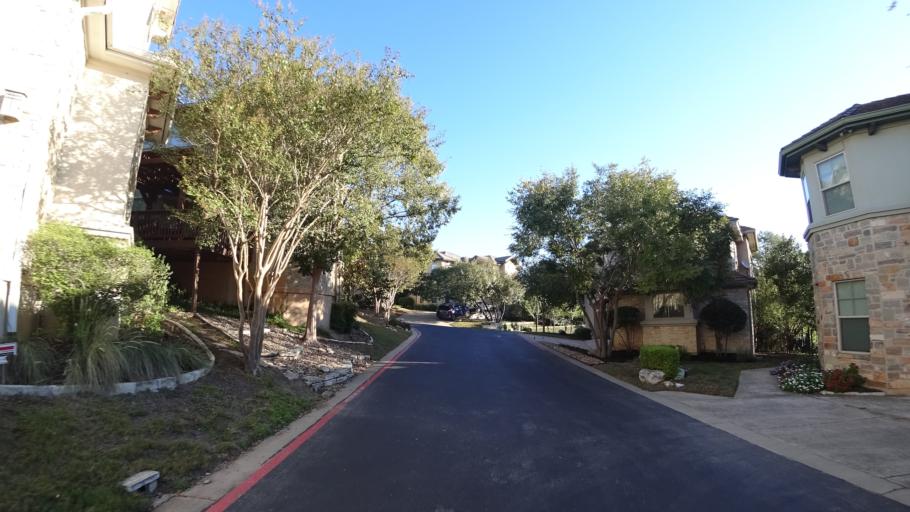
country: US
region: Texas
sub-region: Travis County
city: West Lake Hills
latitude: 30.3254
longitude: -97.8101
